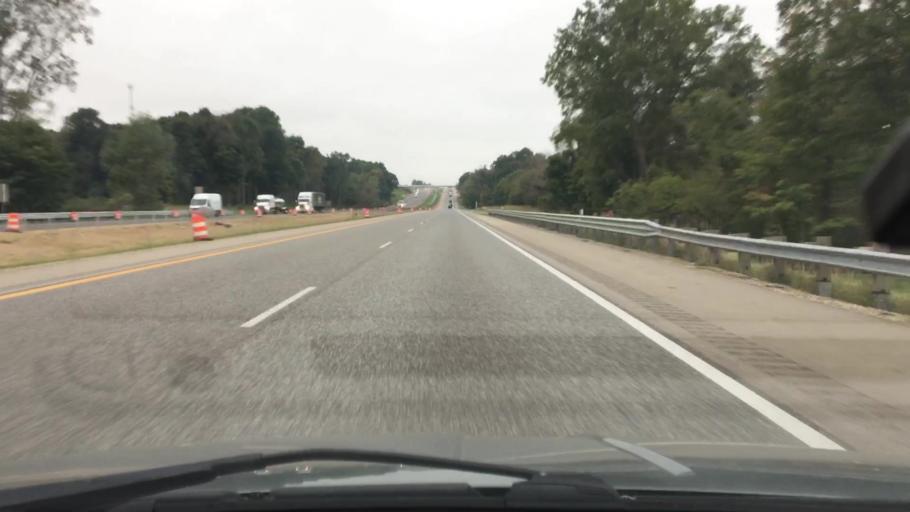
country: US
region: Michigan
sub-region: Van Buren County
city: Decatur
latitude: 42.1965
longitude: -86.0391
